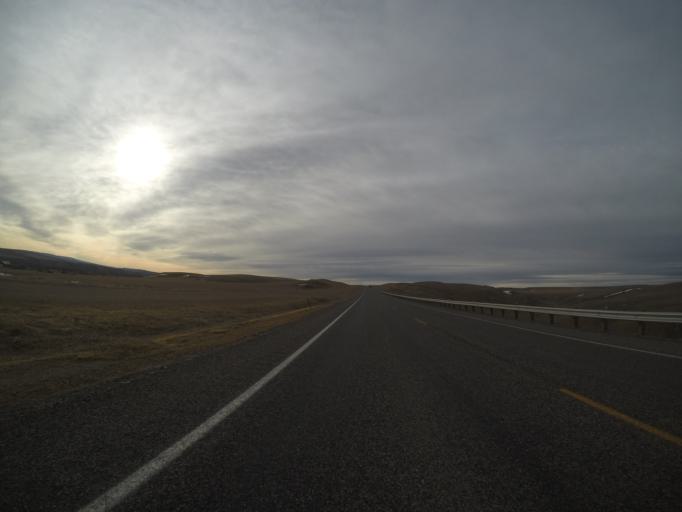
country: US
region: Montana
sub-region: Yellowstone County
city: Laurel
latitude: 45.5711
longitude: -108.8483
